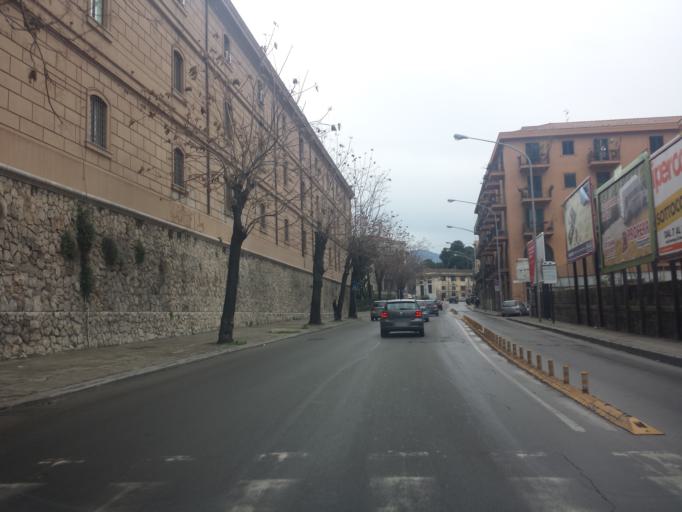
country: IT
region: Sicily
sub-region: Palermo
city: Palermo
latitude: 38.1135
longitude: 13.3524
